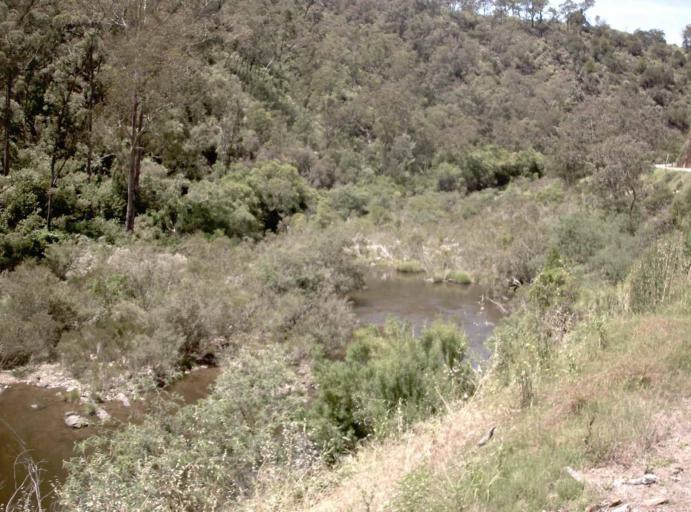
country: AU
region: Victoria
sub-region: East Gippsland
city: Lakes Entrance
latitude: -37.5280
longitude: 147.8507
